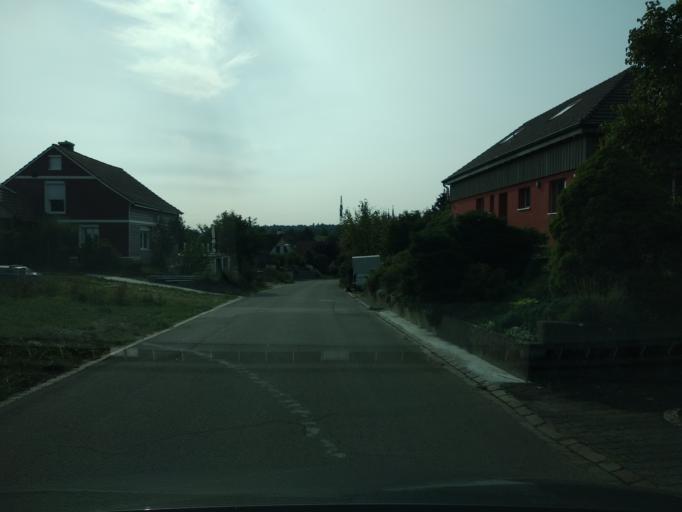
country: DE
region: Baden-Wuerttemberg
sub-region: Freiburg Region
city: Busingen
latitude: 47.6582
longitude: 8.6971
